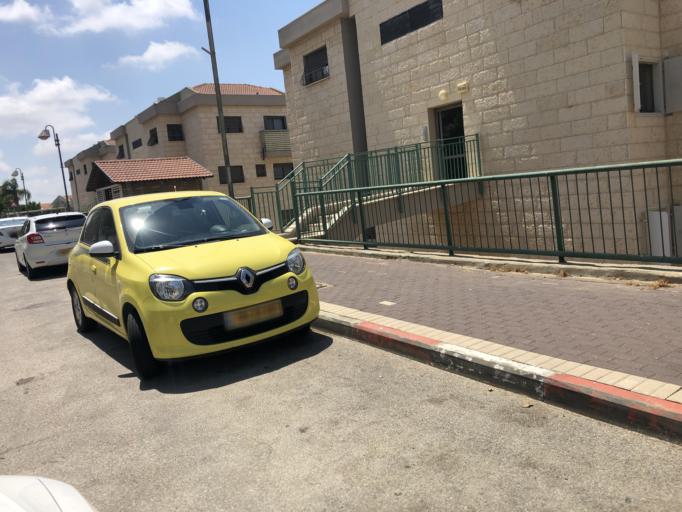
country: IL
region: Haifa
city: Daliyat el Karmil
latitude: 32.6402
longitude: 35.0902
